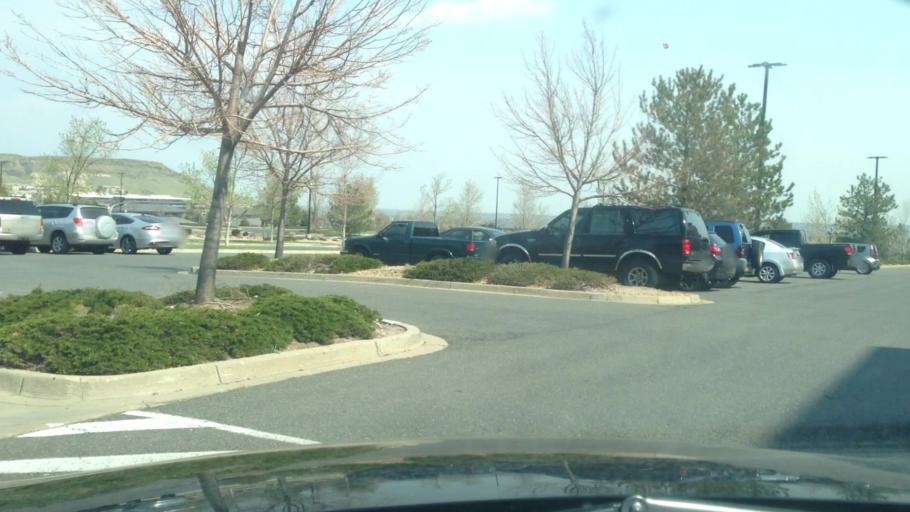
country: US
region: Colorado
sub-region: Jefferson County
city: West Pleasant View
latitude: 39.7329
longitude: -105.1548
